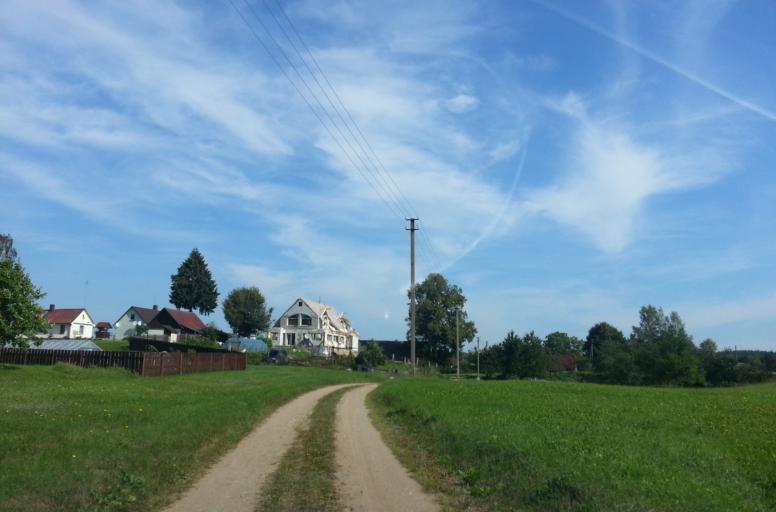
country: LT
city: Grigiskes
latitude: 54.7481
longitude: 25.0228
